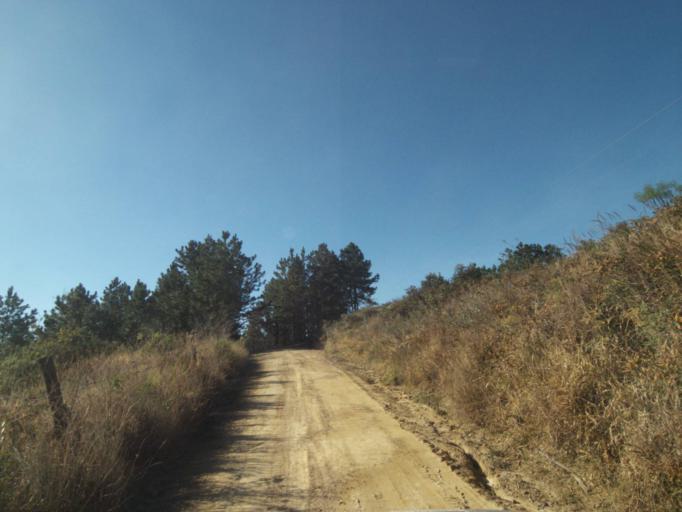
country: BR
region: Parana
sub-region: Tibagi
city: Tibagi
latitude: -24.5702
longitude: -50.4717
